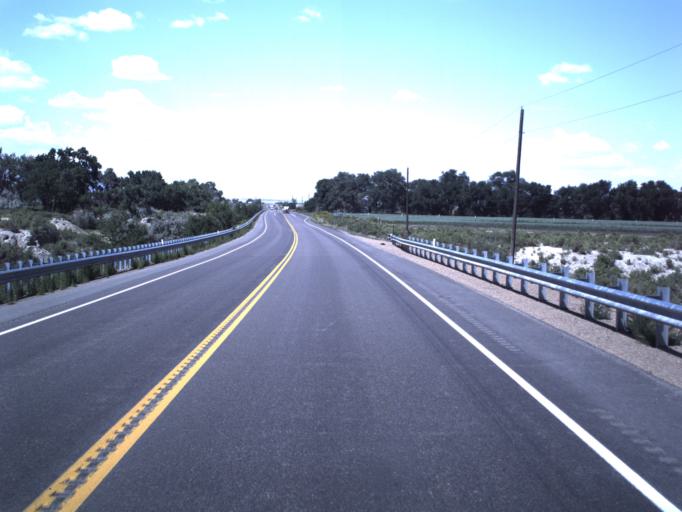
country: US
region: Utah
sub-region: Emery County
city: Huntington
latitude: 39.3011
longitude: -110.9642
